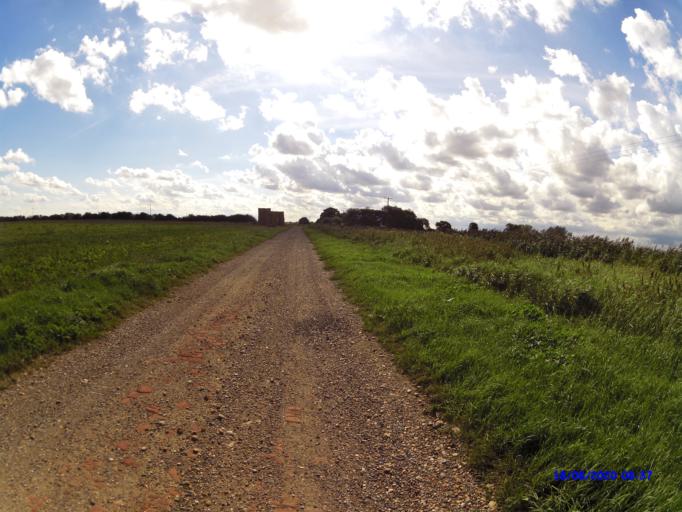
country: GB
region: England
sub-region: Cambridgeshire
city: Ramsey
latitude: 52.4961
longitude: -0.0902
